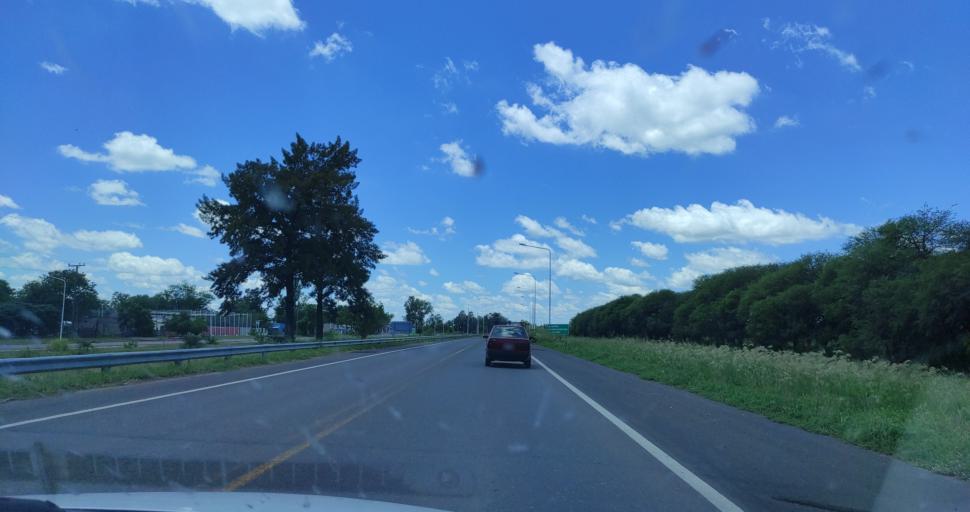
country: AR
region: Chaco
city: Avia Terai
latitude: -26.7034
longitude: -60.7324
